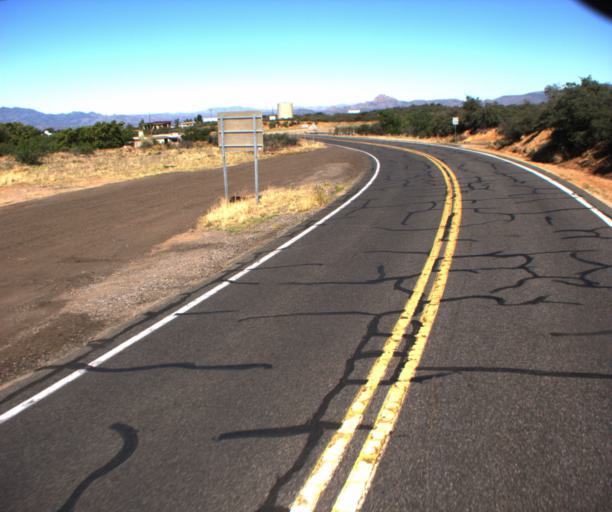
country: US
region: Arizona
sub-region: Yavapai County
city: Prescott
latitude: 34.4276
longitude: -112.5812
